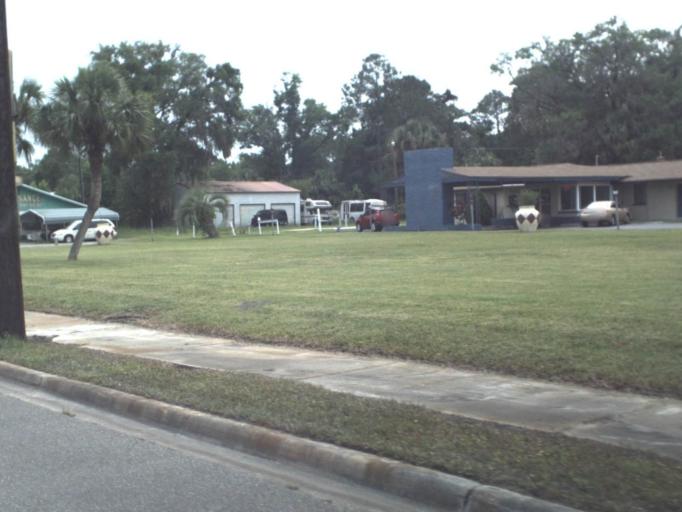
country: US
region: Florida
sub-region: Bradford County
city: Starke
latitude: 29.9627
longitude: -82.1050
